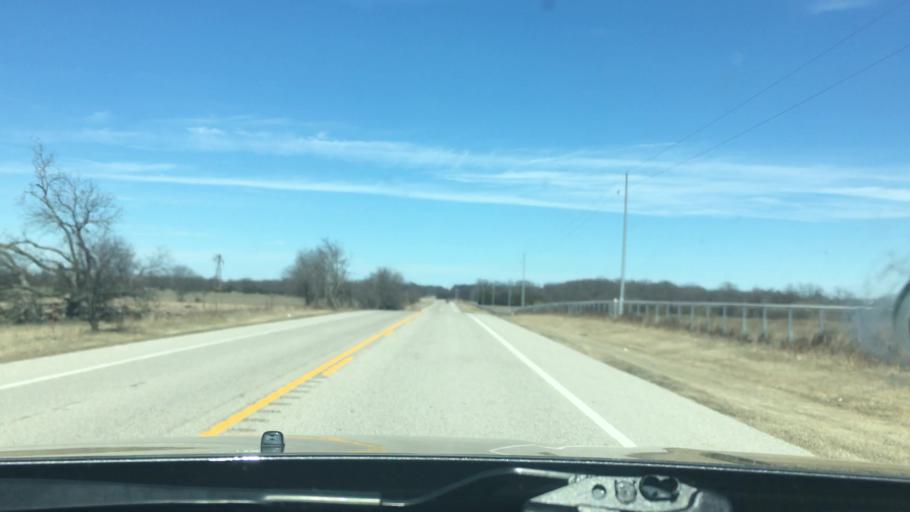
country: US
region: Oklahoma
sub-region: Murray County
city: Sulphur
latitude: 34.3806
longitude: -96.9508
